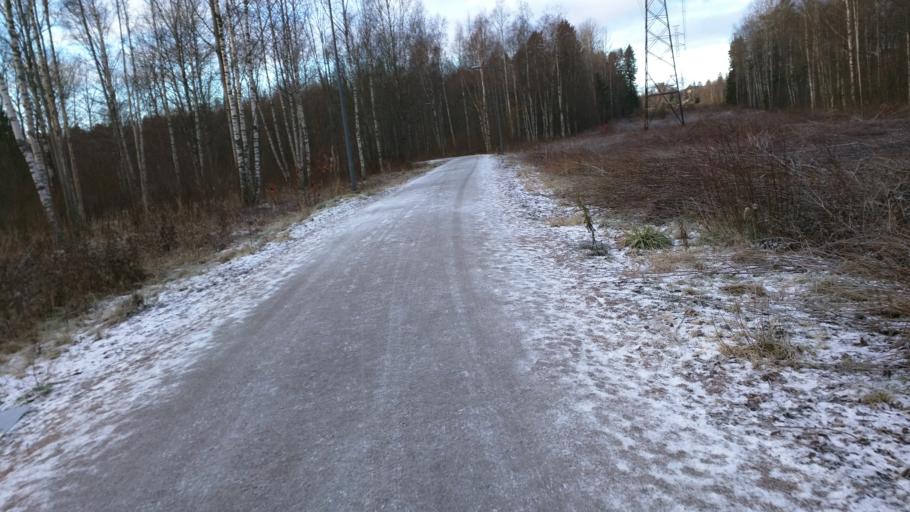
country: FI
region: Uusimaa
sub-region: Helsinki
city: Kauniainen
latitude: 60.2409
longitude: 24.7357
